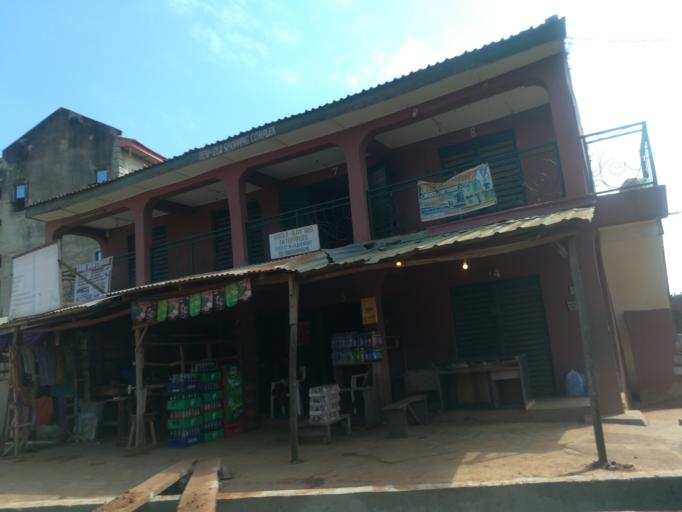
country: NG
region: Oyo
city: Ibadan
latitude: 7.4169
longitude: 3.9772
